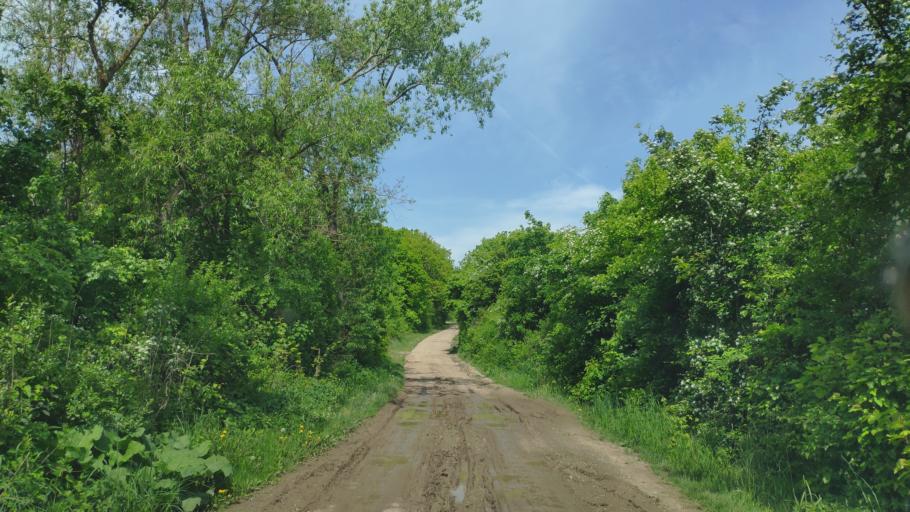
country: SK
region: Kosicky
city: Secovce
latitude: 48.6878
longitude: 21.6051
